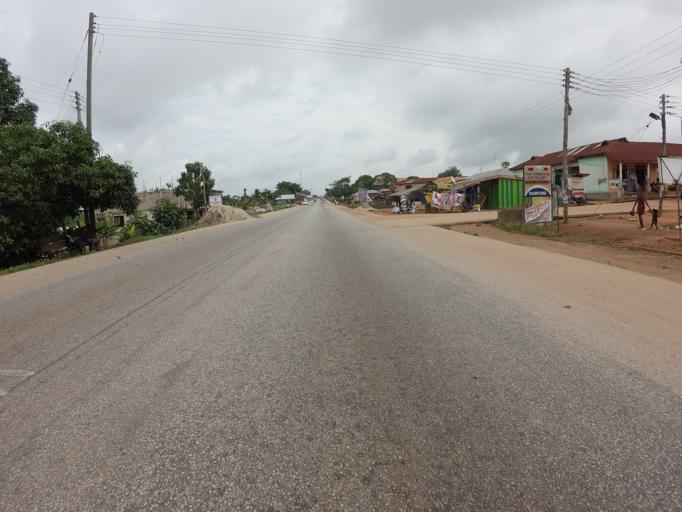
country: GH
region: Ashanti
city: Tafo
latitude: 6.9649
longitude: -1.6797
